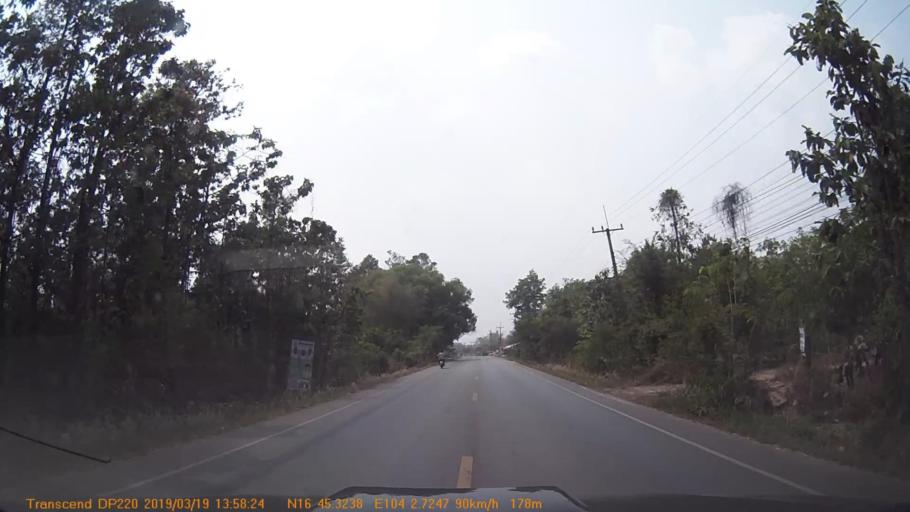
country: TH
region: Kalasin
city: Na Khu
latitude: 16.7556
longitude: 104.0450
